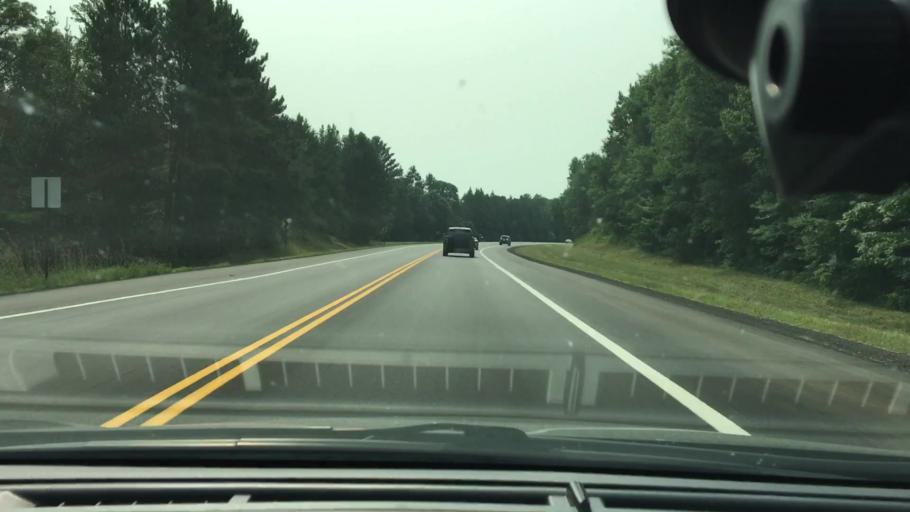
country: US
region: Minnesota
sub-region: Crow Wing County
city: Brainerd
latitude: 46.4141
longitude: -94.1771
